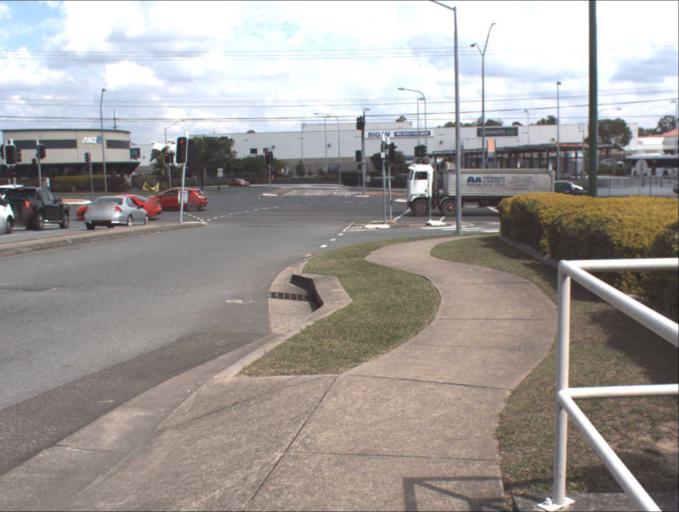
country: AU
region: Queensland
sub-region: Brisbane
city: Sunnybank Hills
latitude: -27.6605
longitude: 153.0425
